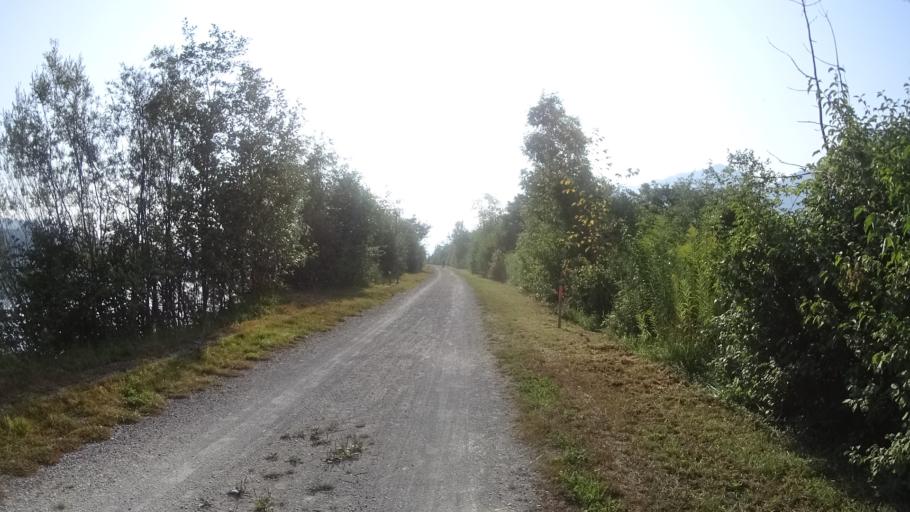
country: AT
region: Carinthia
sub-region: Politischer Bezirk Klagenfurt Land
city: Feistritz im Rosental
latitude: 46.5291
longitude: 14.1510
